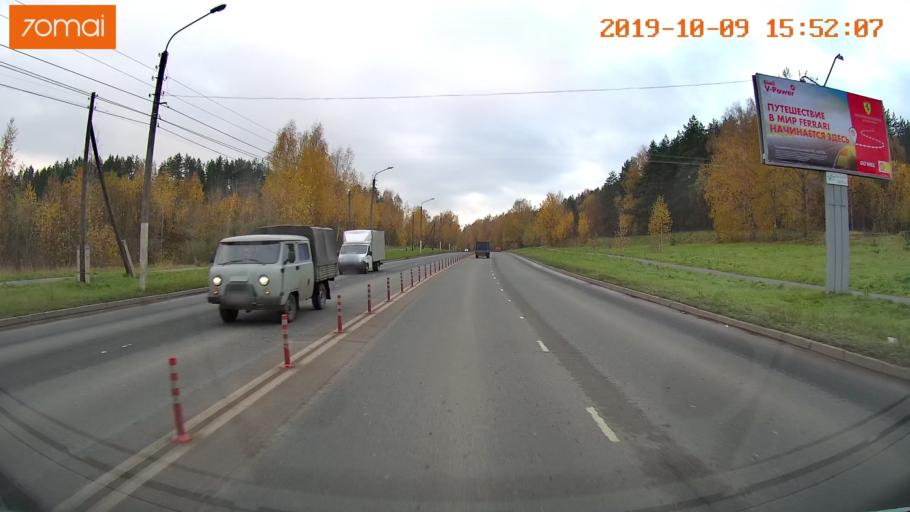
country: RU
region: Kostroma
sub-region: Kostromskoy Rayon
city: Kostroma
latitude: 57.7920
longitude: 40.9720
